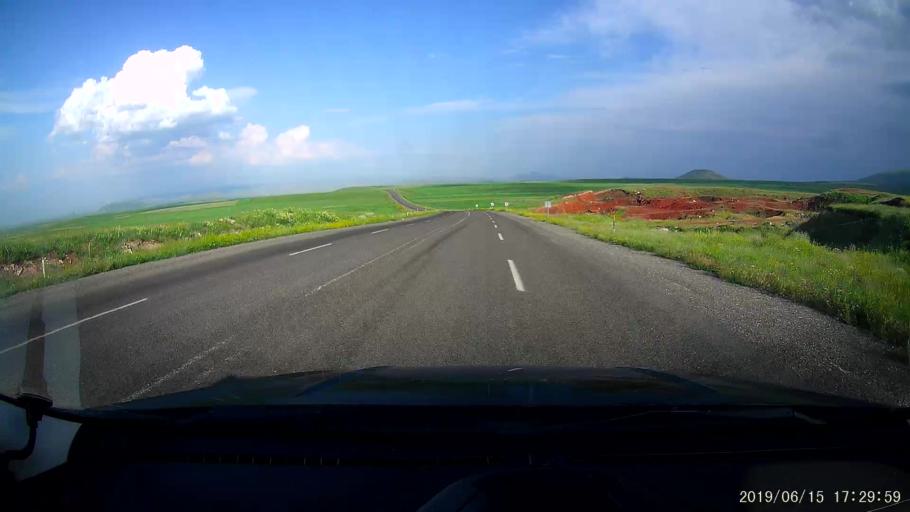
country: TR
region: Kars
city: Basgedikler
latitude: 40.5856
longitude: 43.4612
